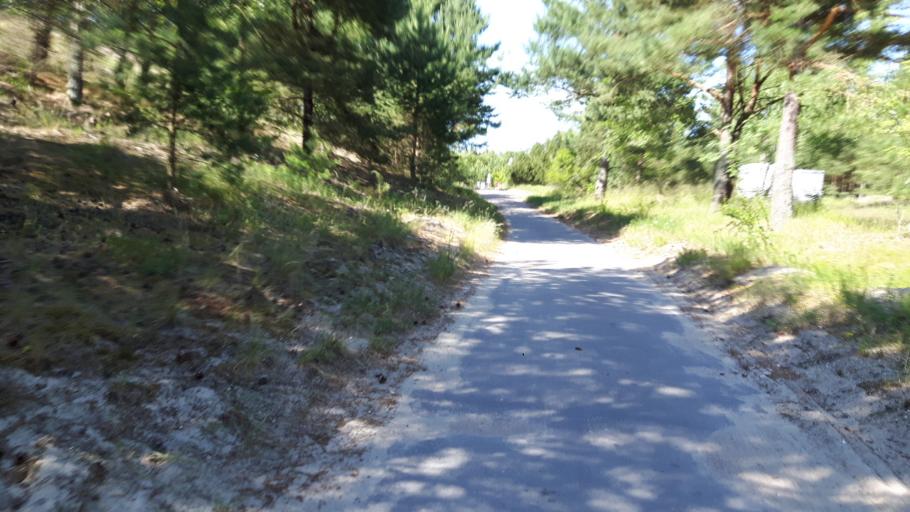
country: LT
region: Klaipedos apskritis
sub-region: Klaipeda
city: Klaipeda
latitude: 55.6969
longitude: 21.1020
